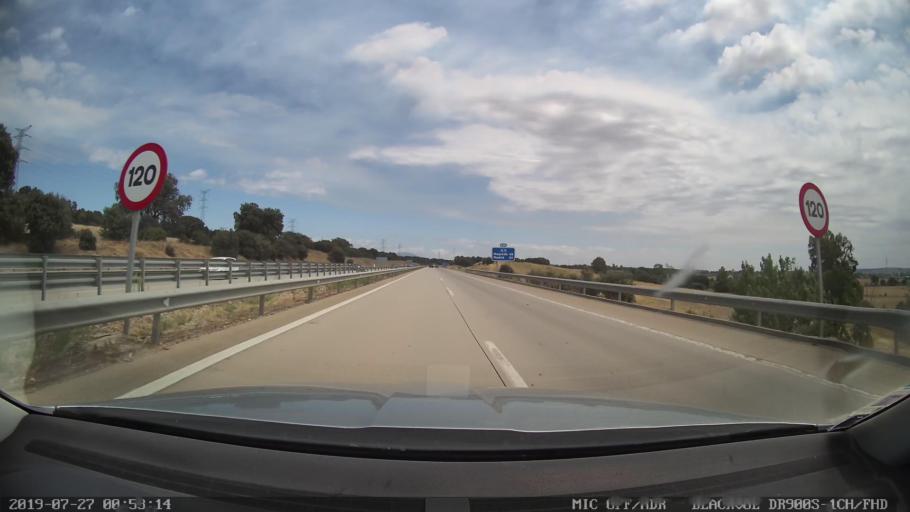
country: ES
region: Castille-La Mancha
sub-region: Province of Toledo
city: Mejorada
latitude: 39.9663
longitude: -4.8973
